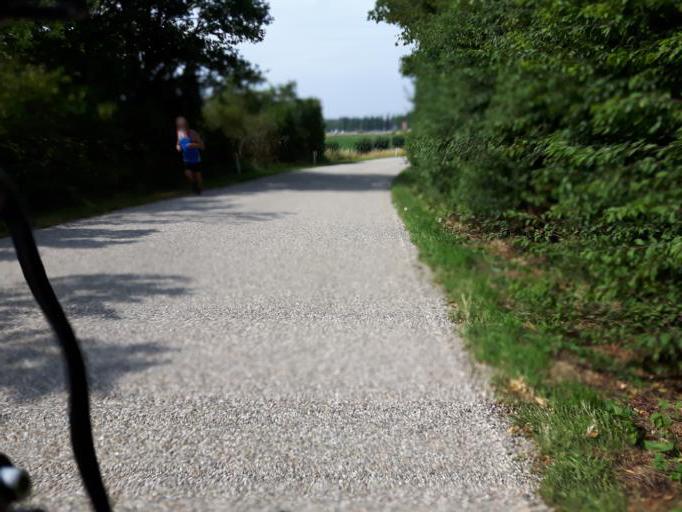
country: NL
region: Zeeland
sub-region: Gemeente Middelburg
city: Middelburg
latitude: 51.4767
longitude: 3.6307
